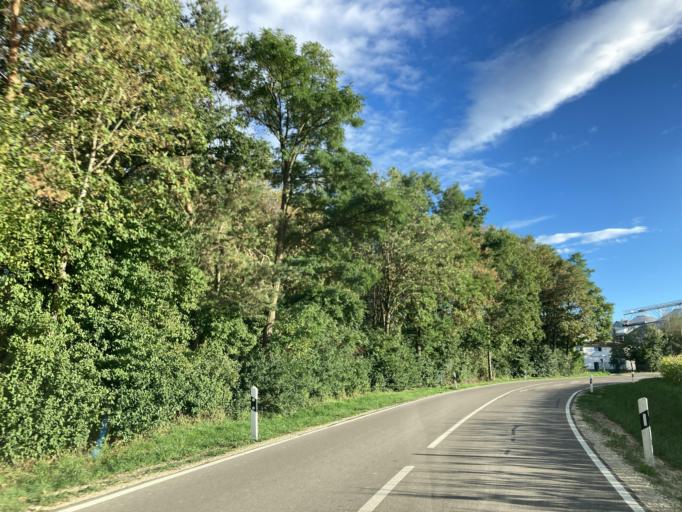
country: DE
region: Bavaria
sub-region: Swabia
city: Ziertheim
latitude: 48.6623
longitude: 10.4043
